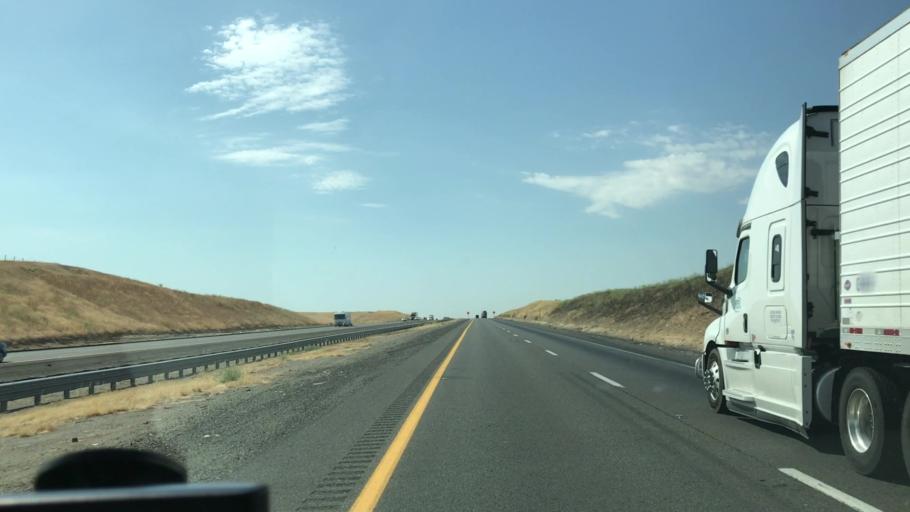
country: US
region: California
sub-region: Merced County
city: Gustine
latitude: 37.1762
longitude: -121.0627
